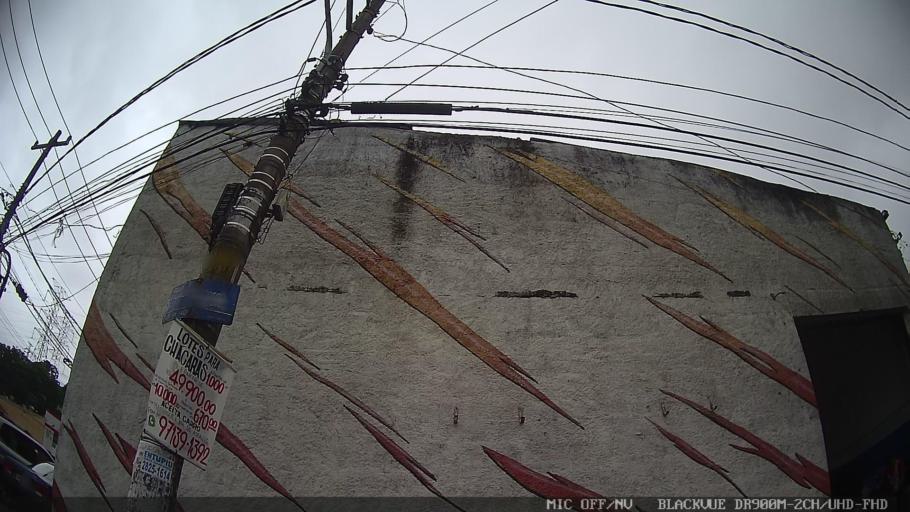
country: BR
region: Sao Paulo
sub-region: Osasco
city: Osasco
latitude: -23.4954
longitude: -46.7463
